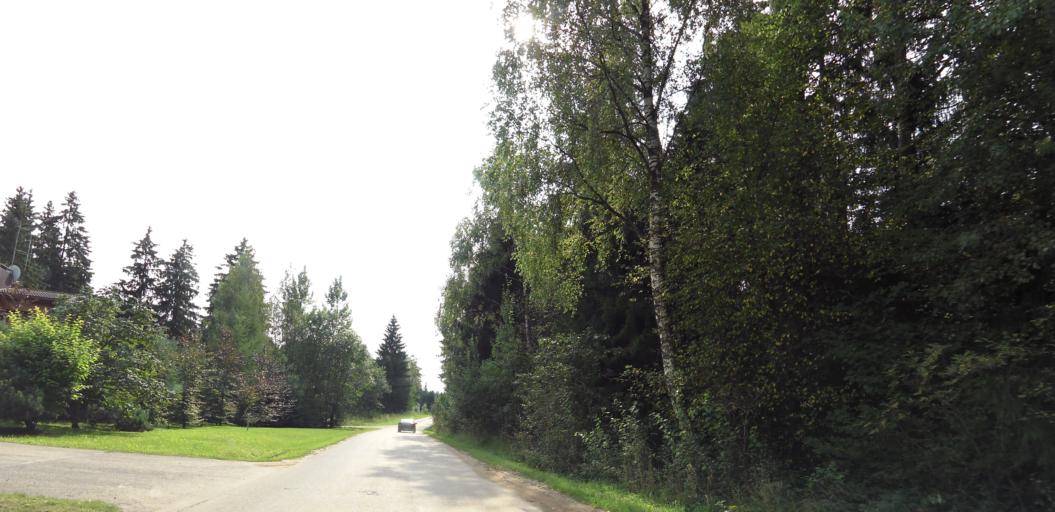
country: LT
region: Vilnius County
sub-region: Vilnius
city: Fabijoniskes
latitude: 54.7503
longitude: 25.2451
